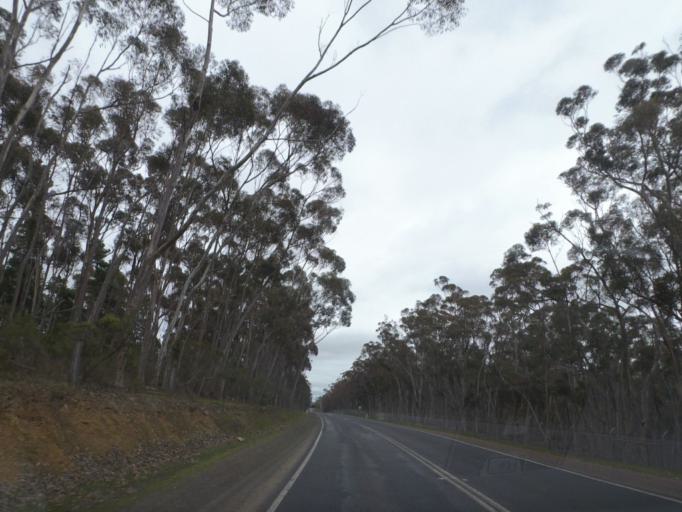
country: AU
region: Victoria
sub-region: Nillumbik
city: Doreen
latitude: -37.5695
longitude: 145.1354
